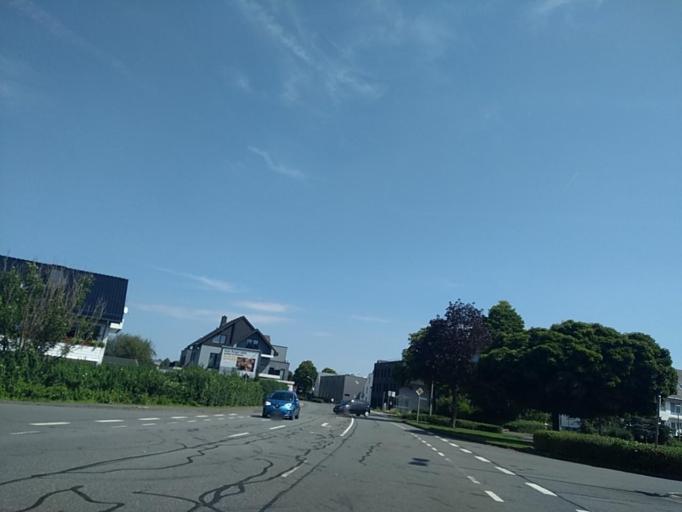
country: DE
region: North Rhine-Westphalia
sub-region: Regierungsbezirk Arnsberg
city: Brilon
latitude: 51.3962
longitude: 8.5788
